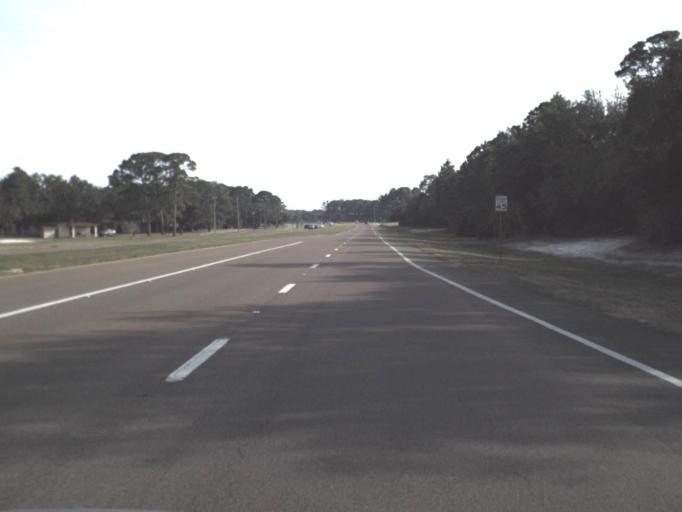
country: US
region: Florida
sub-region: Bay County
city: Tyndall Air Force Base
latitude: 30.0942
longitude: -85.6119
